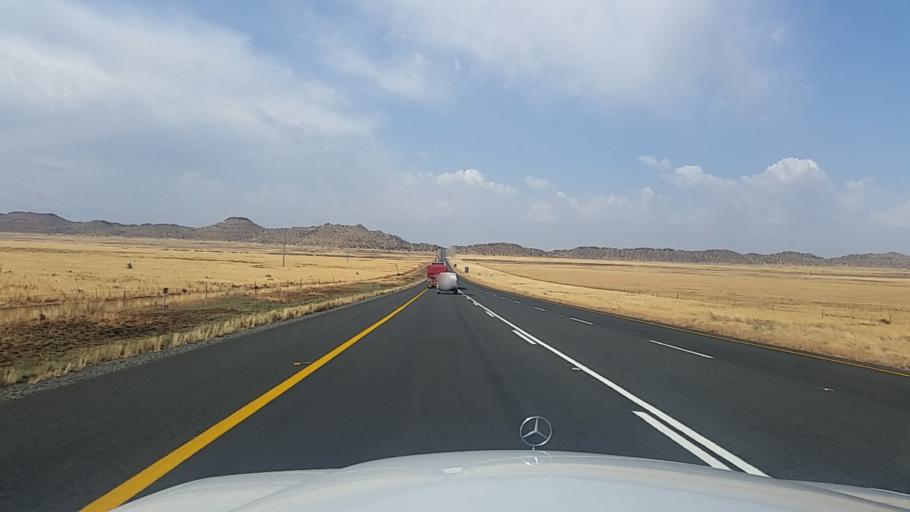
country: ZA
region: Orange Free State
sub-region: Xhariep District Municipality
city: Trompsburg
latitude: -30.3755
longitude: 25.6801
